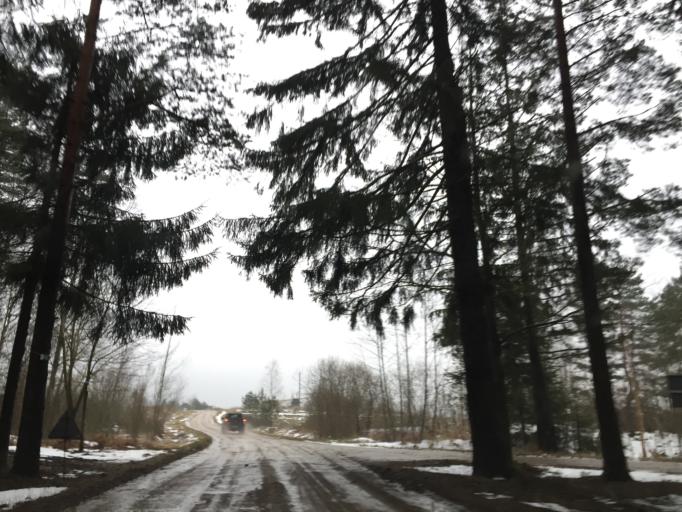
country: LV
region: Incukalns
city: Vangazi
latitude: 57.1230
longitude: 24.5706
